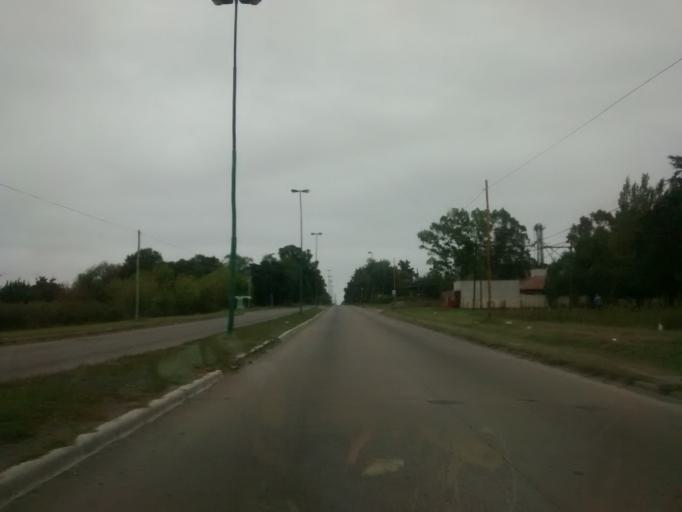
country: AR
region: Buenos Aires
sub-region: Partido de La Plata
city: La Plata
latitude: -34.9754
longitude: -58.0265
